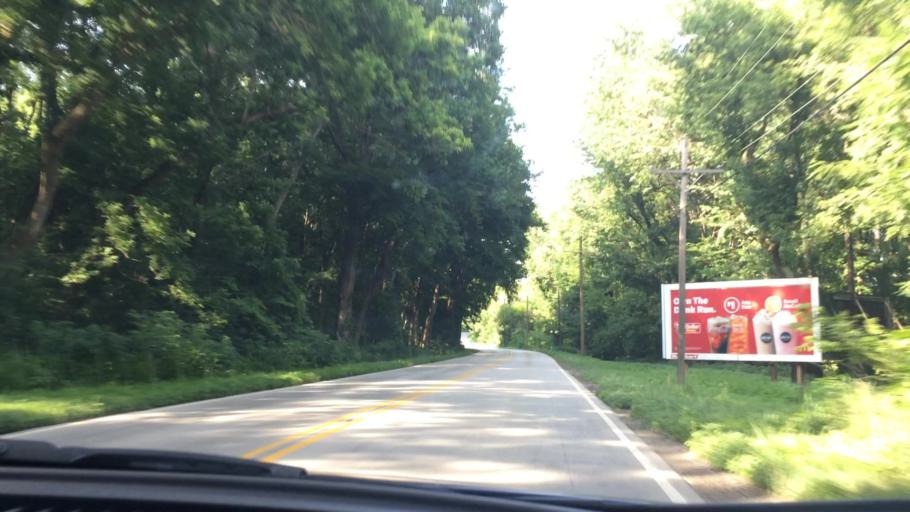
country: US
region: Indiana
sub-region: Tippecanoe County
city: West Lafayette
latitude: 40.4648
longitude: -86.8884
